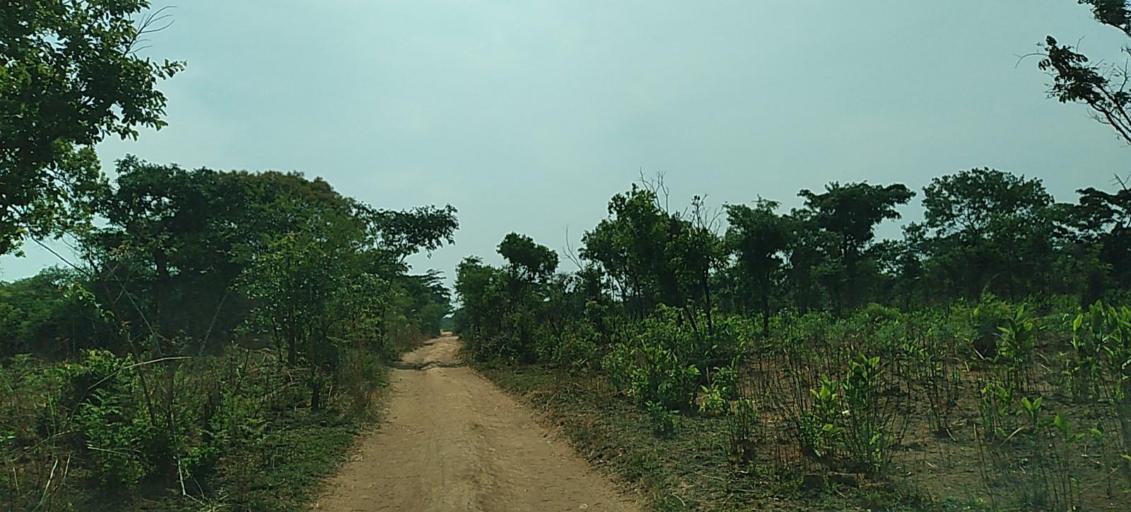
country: ZM
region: Copperbelt
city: Ndola
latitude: -13.2100
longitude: 28.7417
